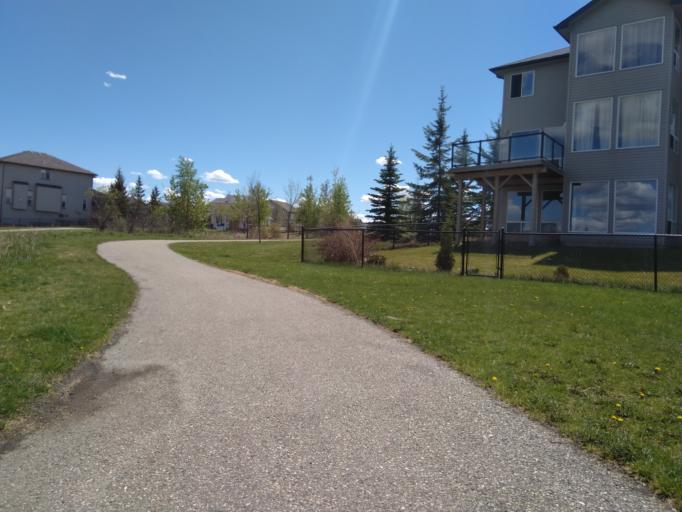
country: CA
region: Alberta
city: Chestermere
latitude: 51.0325
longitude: -113.8383
